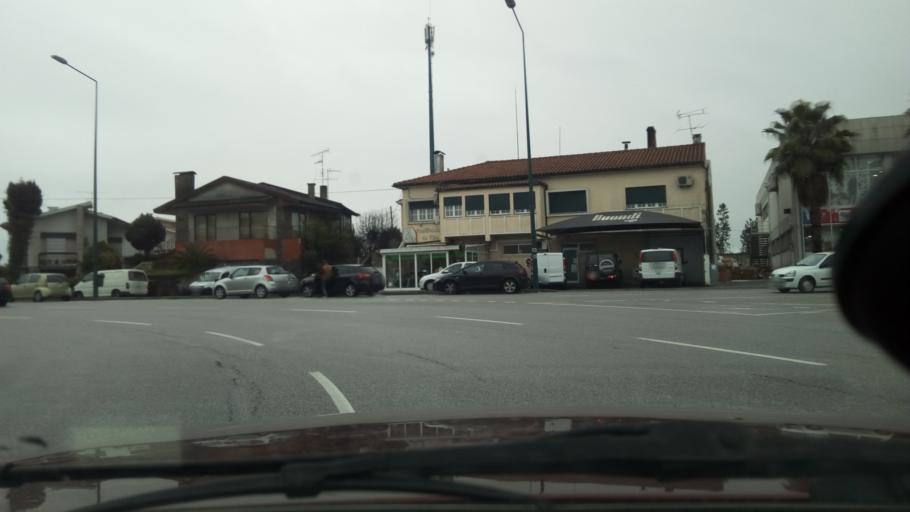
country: PT
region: Viseu
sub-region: Viseu
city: Rio de Loba
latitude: 40.6530
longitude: -7.8898
